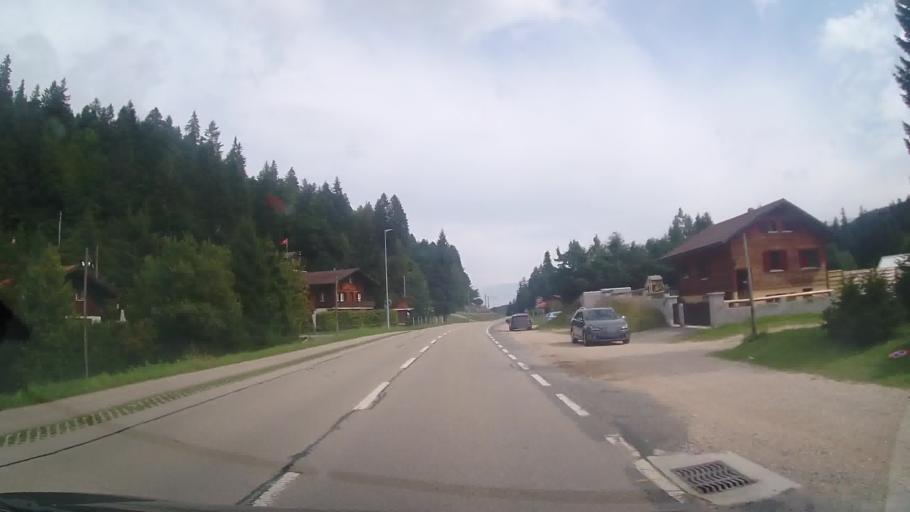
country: CH
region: Vaud
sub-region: Nyon District
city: Saint-Cergue
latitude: 46.4515
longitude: 6.1253
